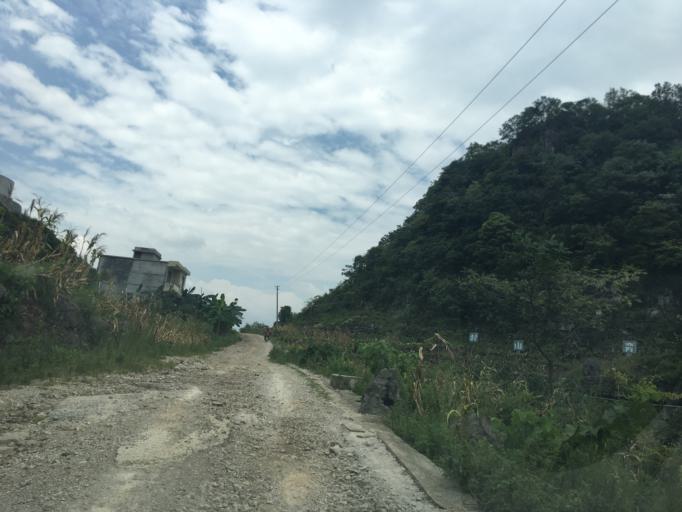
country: CN
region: Guangxi Zhuangzu Zizhiqu
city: Xinzhou
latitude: 25.2941
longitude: 105.6315
